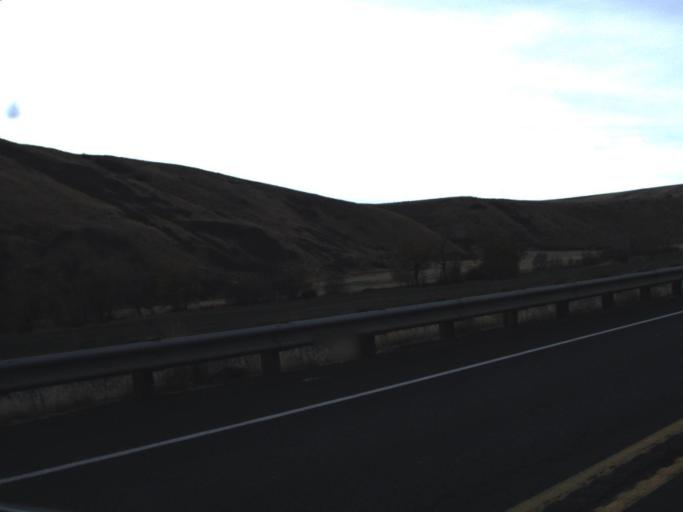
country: US
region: Washington
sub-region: Garfield County
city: Pomeroy
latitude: 46.4675
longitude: -117.4976
